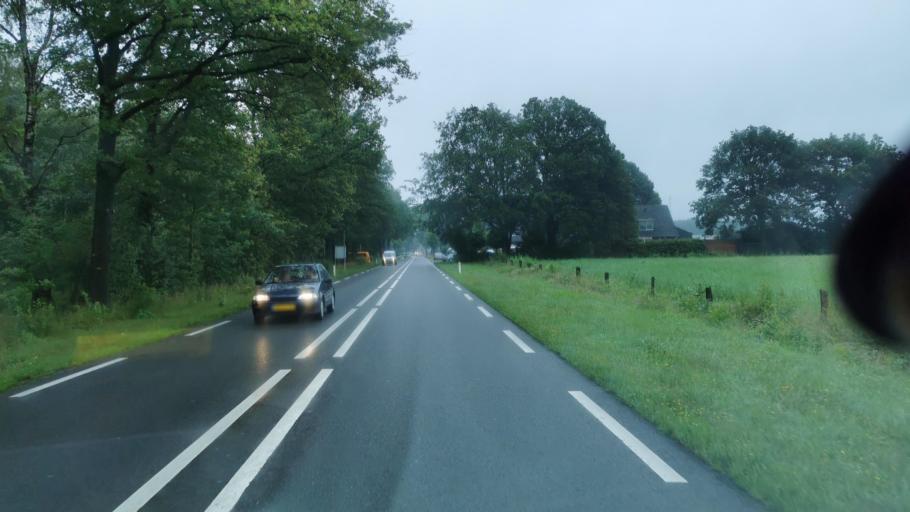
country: NL
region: Overijssel
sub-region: Gemeente Losser
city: Losser
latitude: 52.2458
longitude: 7.0284
